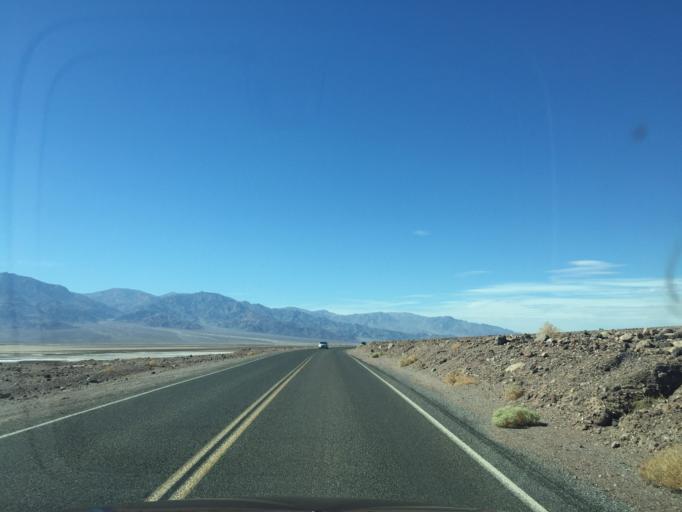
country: US
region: Nevada
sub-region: Nye County
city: Beatty
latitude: 36.2762
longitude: -116.7968
